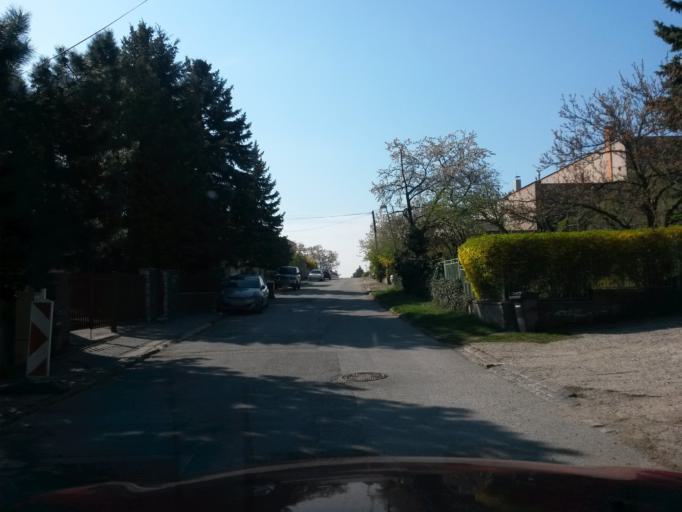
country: SK
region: Kosicky
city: Kosice
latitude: 48.7526
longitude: 21.2414
